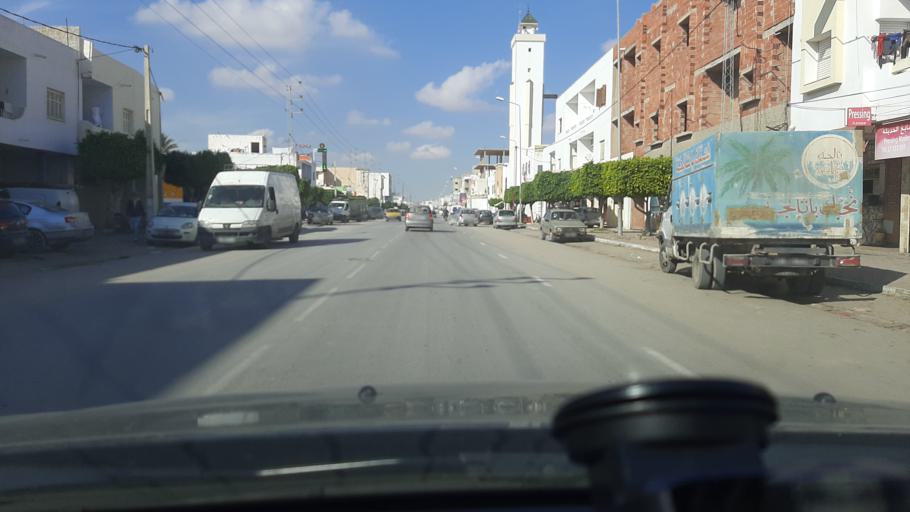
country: TN
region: Safaqis
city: Sfax
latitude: 34.7927
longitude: 10.7158
